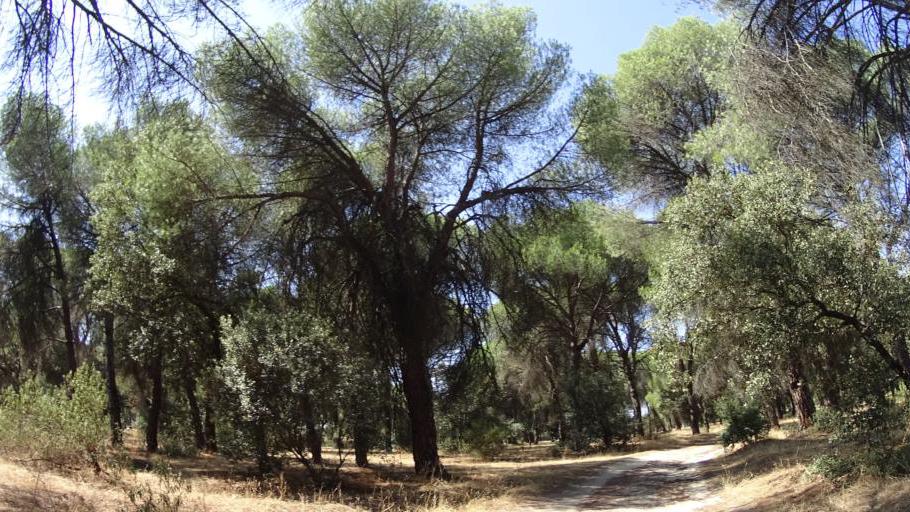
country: ES
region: Madrid
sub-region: Provincia de Madrid
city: Boadilla del Monte
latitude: 40.4353
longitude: -3.8734
